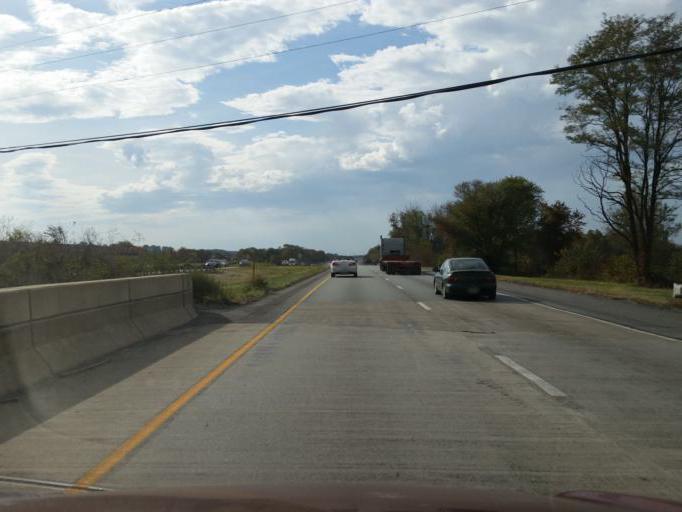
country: US
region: Pennsylvania
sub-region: Lancaster County
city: Mount Joy
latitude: 40.1303
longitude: -76.4935
